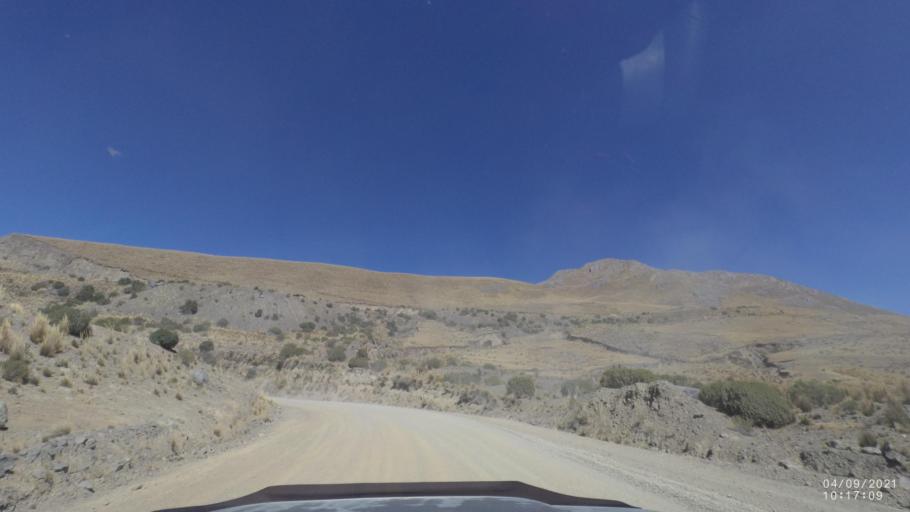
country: BO
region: Cochabamba
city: Sipe Sipe
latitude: -17.3192
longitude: -66.4217
